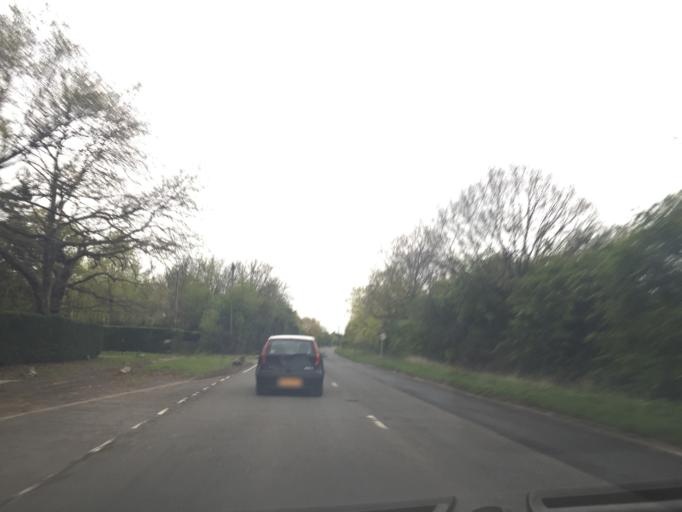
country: GB
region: England
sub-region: Greater London
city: Collier Row
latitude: 51.6341
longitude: 0.1714
